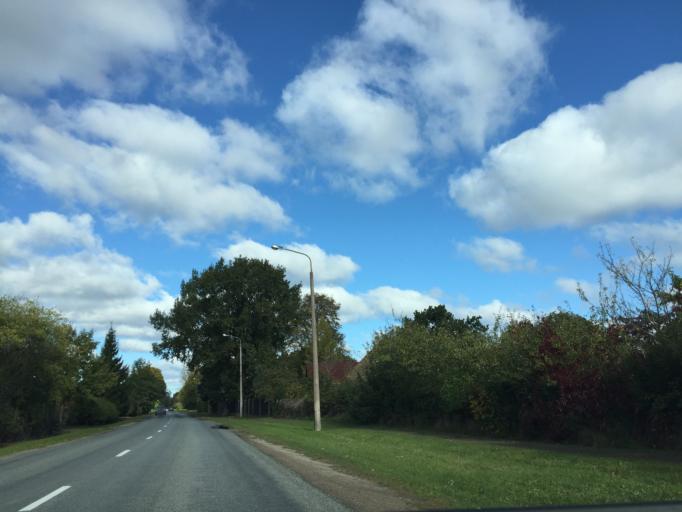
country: LV
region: Tukuma Rajons
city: Engure
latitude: 57.1520
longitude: 23.2307
